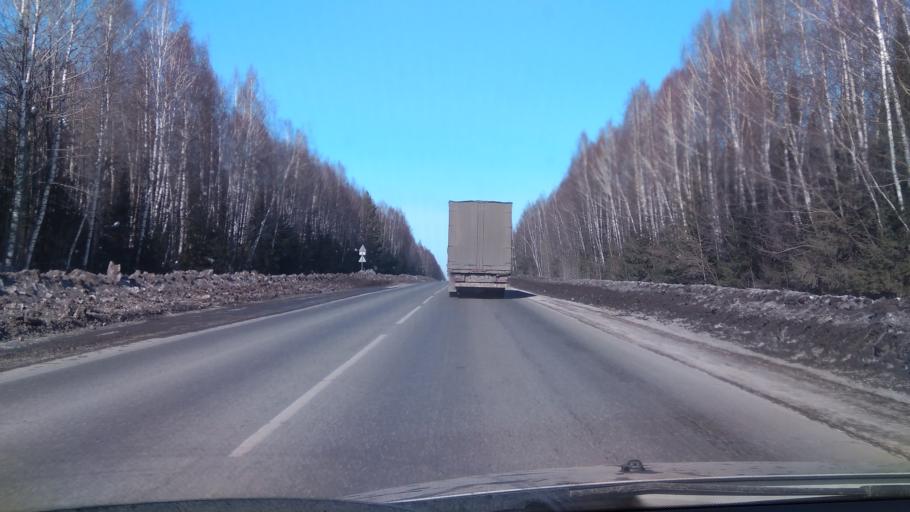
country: RU
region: Perm
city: Kukushtan
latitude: 57.5676
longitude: 56.5667
